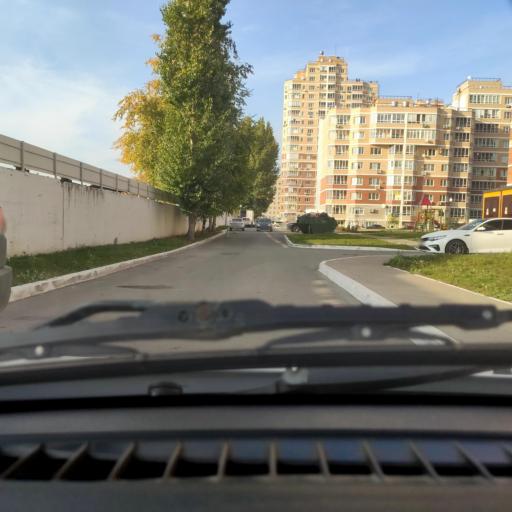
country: RU
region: Samara
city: Tol'yatti
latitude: 53.4984
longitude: 49.4207
